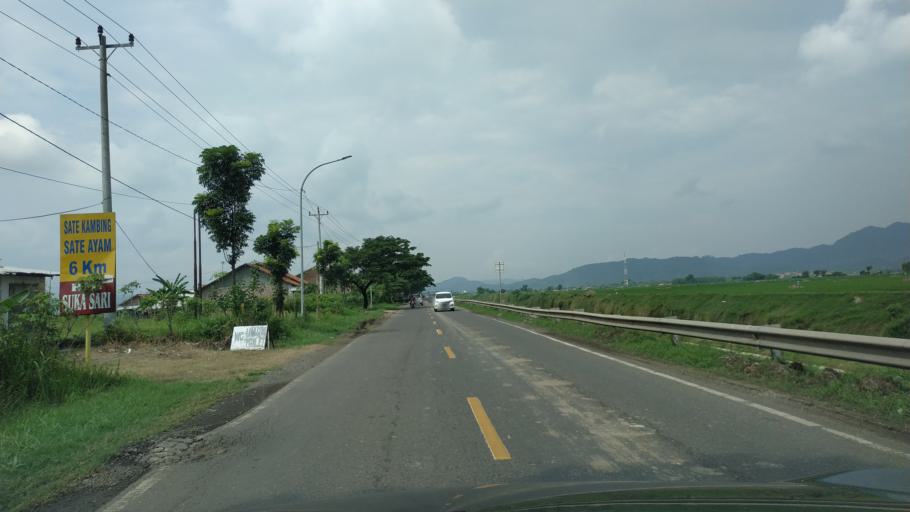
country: ID
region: Central Java
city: Margasari
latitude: -7.0775
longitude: 108.9827
